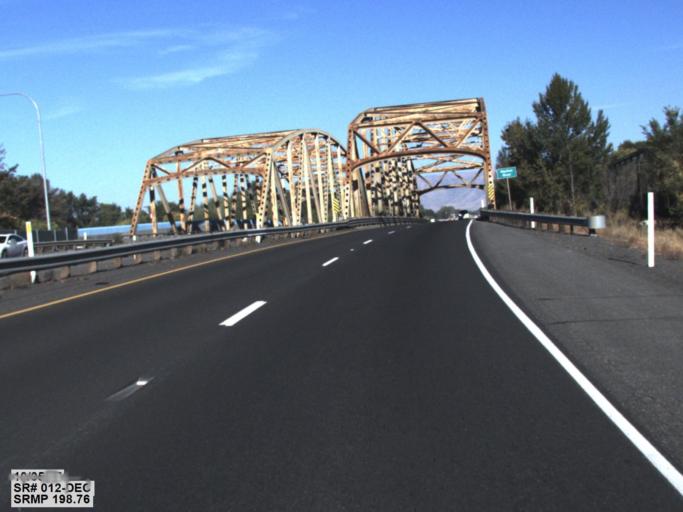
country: US
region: Washington
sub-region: Yakima County
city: Gleed
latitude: 46.6311
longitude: -120.5852
